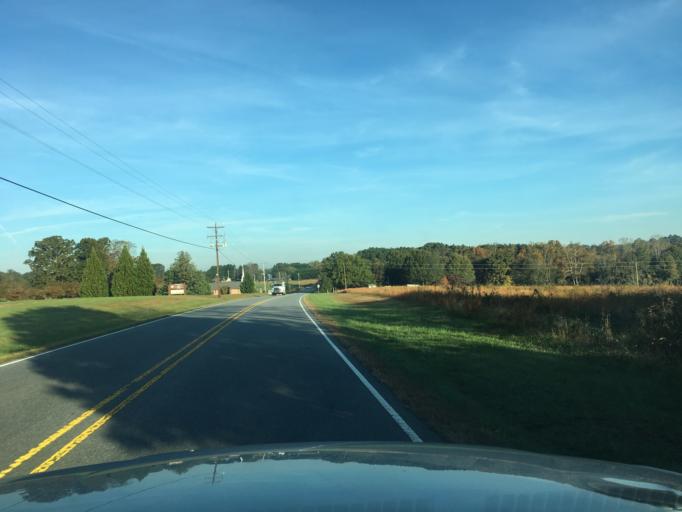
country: US
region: North Carolina
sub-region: Catawba County
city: Newton
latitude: 35.6258
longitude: -81.2636
